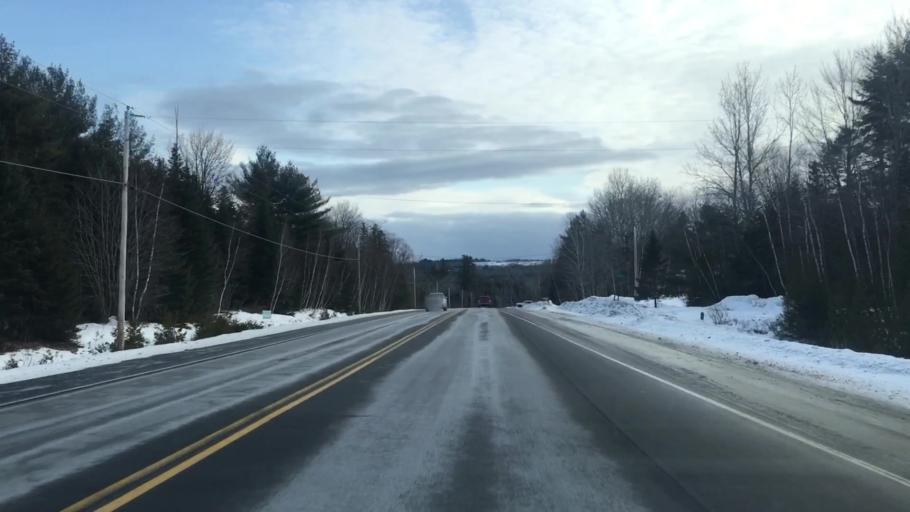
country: US
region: Maine
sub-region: Washington County
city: Machias
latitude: 44.9491
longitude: -67.6922
